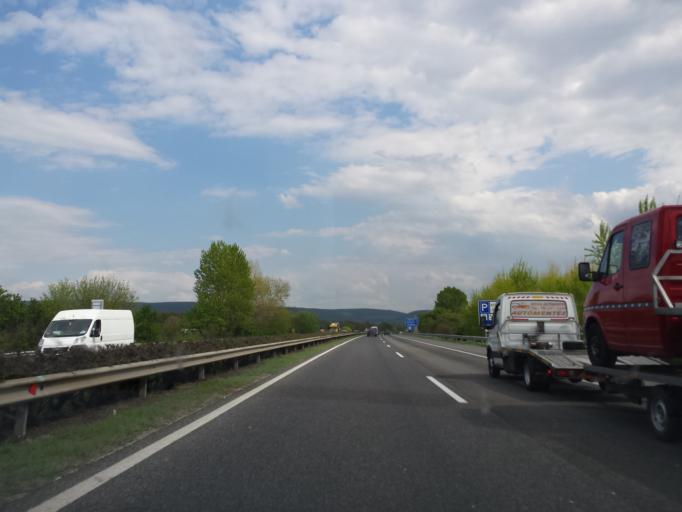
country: HU
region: Komarom-Esztergom
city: Tata
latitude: 47.6228
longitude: 18.3236
